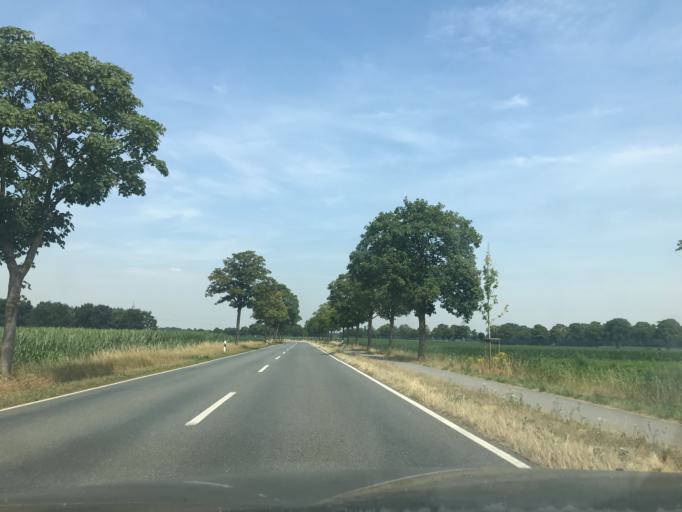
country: DE
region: North Rhine-Westphalia
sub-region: Regierungsbezirk Dusseldorf
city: Issum
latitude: 51.5022
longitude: 6.4199
